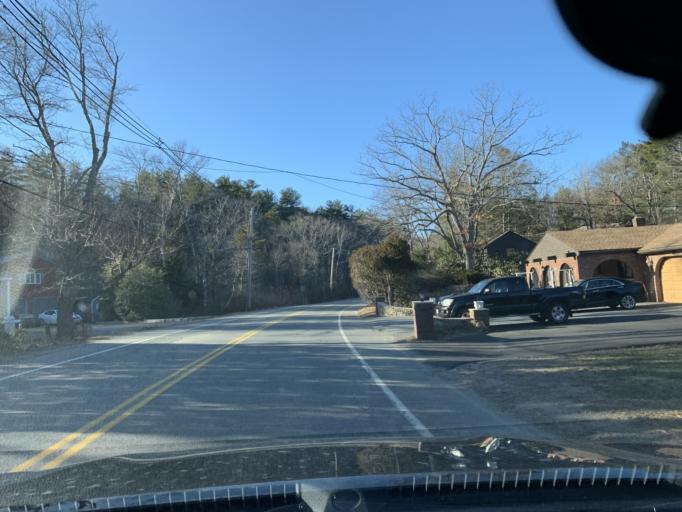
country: US
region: Massachusetts
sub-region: Essex County
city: Essex
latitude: 42.5883
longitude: -70.7885
